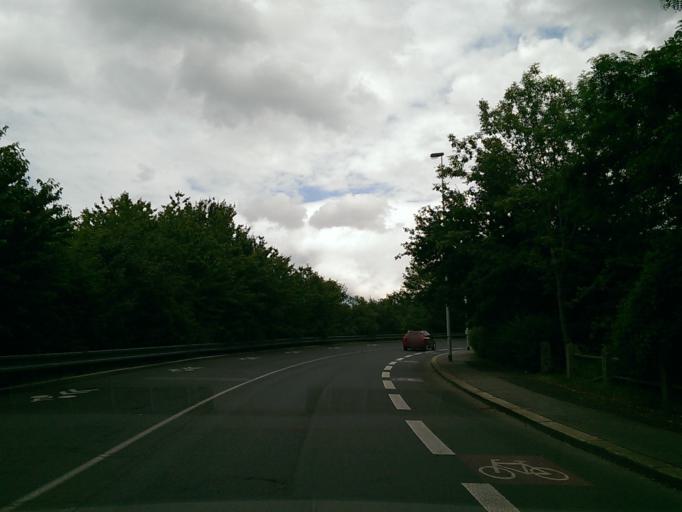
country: CZ
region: Praha
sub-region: Praha 4
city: Hodkovicky
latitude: 50.0319
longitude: 14.4288
